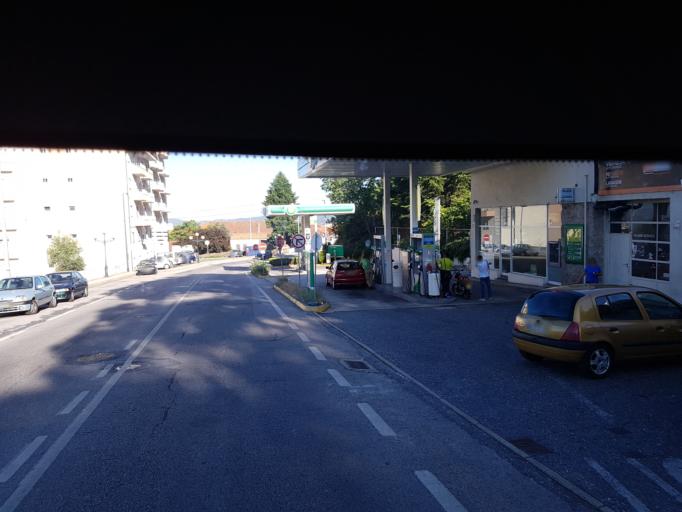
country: PT
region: Castelo Branco
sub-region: Covilha
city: Covilha
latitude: 40.2760
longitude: -7.5061
